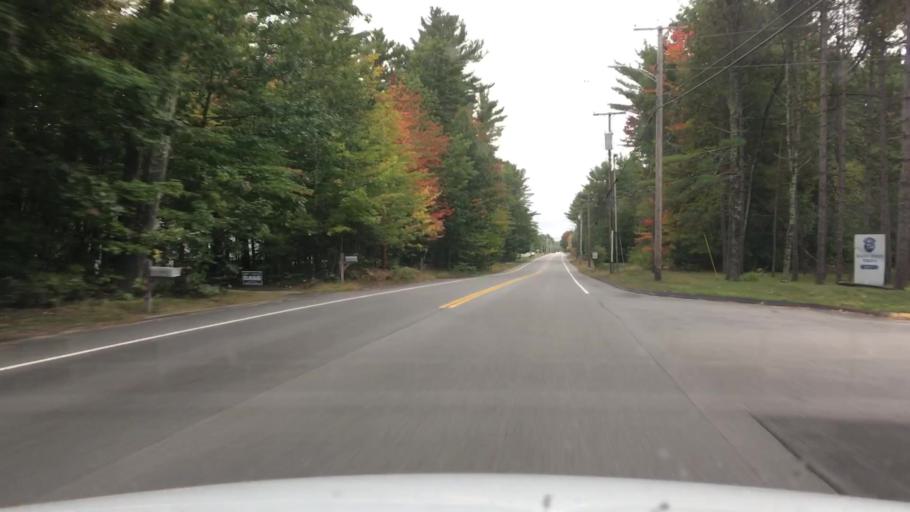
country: US
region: Maine
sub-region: Cumberland County
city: New Gloucester
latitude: 43.9294
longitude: -70.3532
